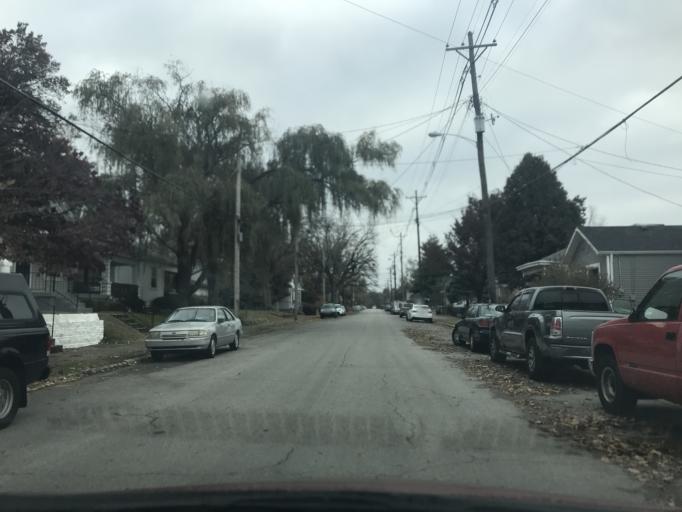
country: US
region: Kentucky
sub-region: Jefferson County
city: Louisville
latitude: 38.2387
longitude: -85.7323
